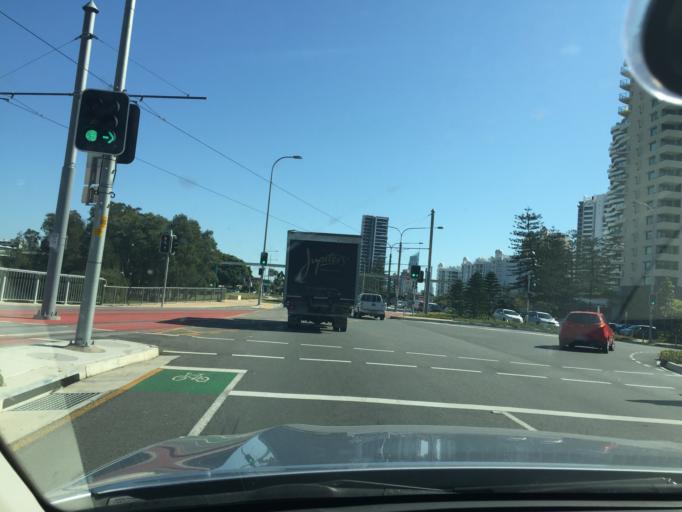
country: AU
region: Queensland
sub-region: Gold Coast
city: Surfers Paradise
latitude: -28.0317
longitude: 153.4305
